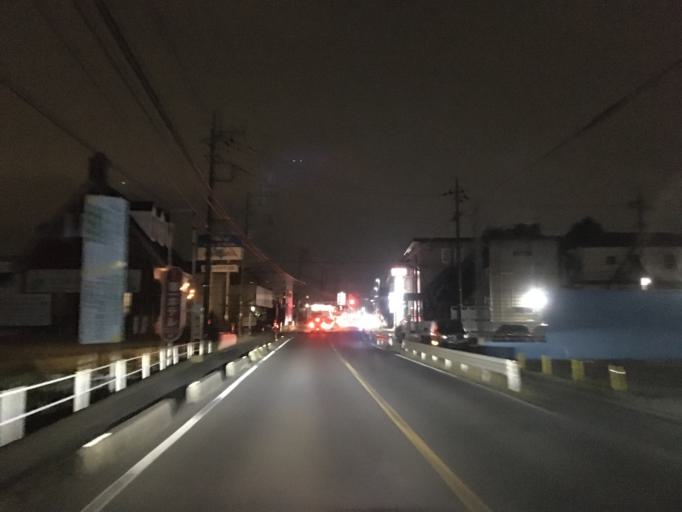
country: JP
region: Saitama
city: Sayama
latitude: 35.8297
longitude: 139.4333
